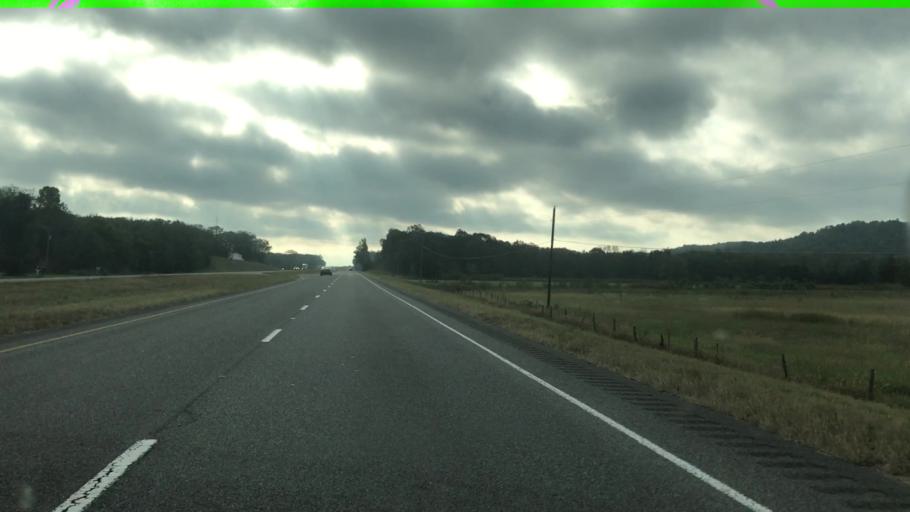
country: US
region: Alabama
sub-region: Morgan County
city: Danville
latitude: 34.4056
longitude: -87.1414
